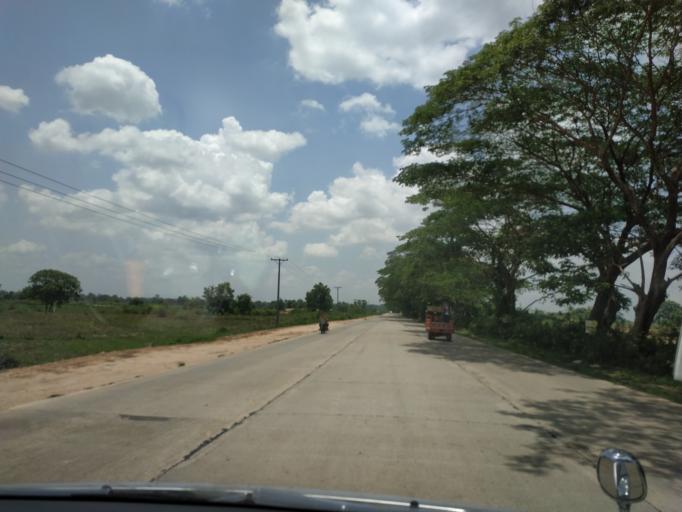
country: MM
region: Bago
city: Bago
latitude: 17.4781
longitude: 96.4997
